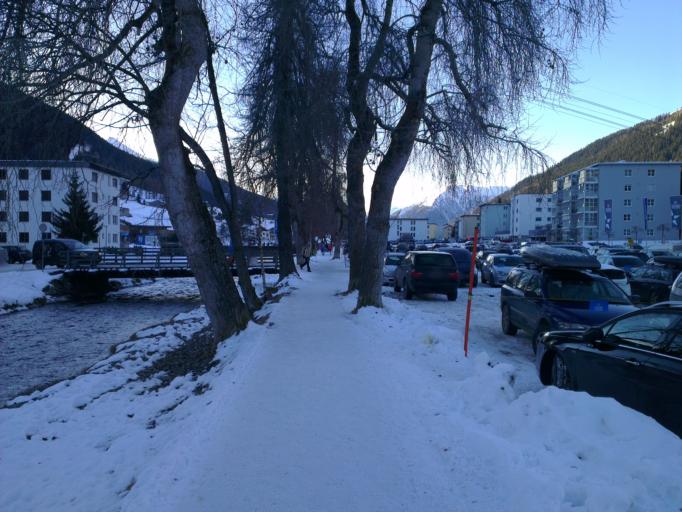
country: CH
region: Grisons
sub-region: Praettigau/Davos District
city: Davos
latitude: 46.7921
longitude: 9.8233
